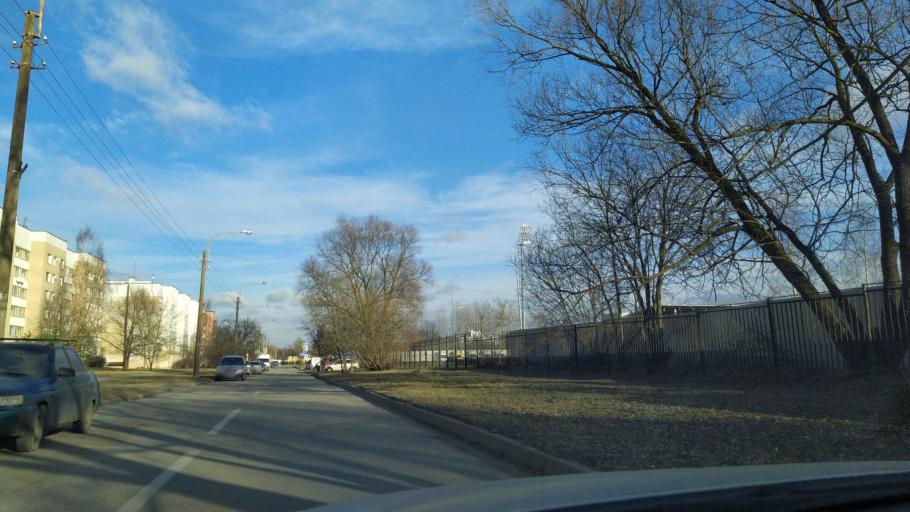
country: RU
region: St.-Petersburg
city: Pushkin
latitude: 59.7321
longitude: 30.4030
